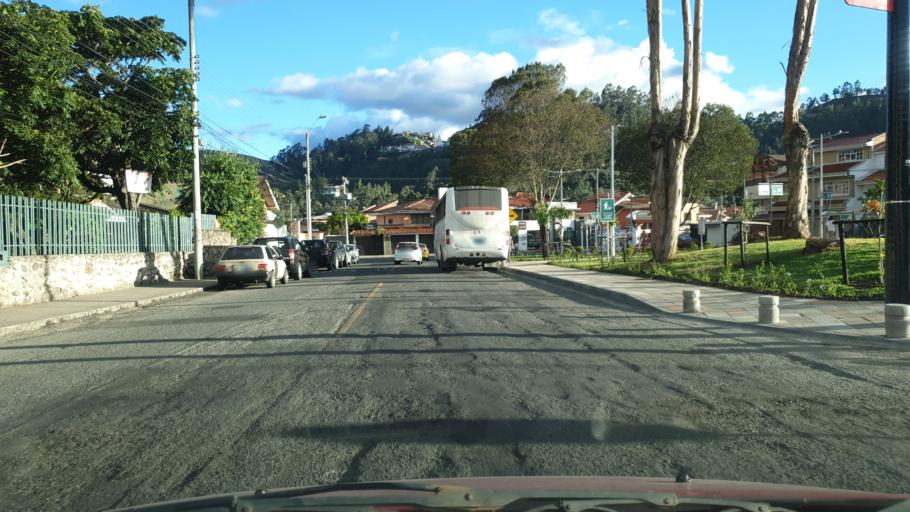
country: EC
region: Azuay
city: Cuenca
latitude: -2.9133
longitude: -79.0146
